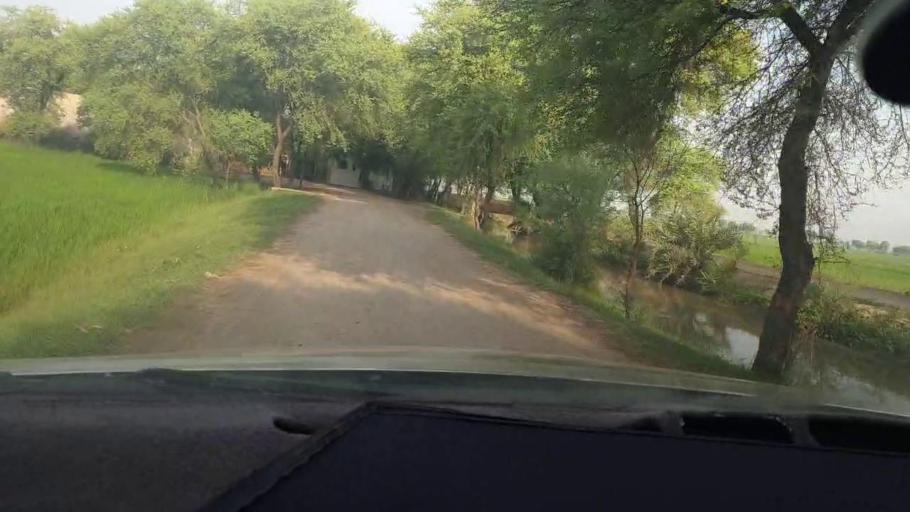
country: PK
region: Sindh
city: Jacobabad
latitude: 28.3094
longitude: 68.4123
